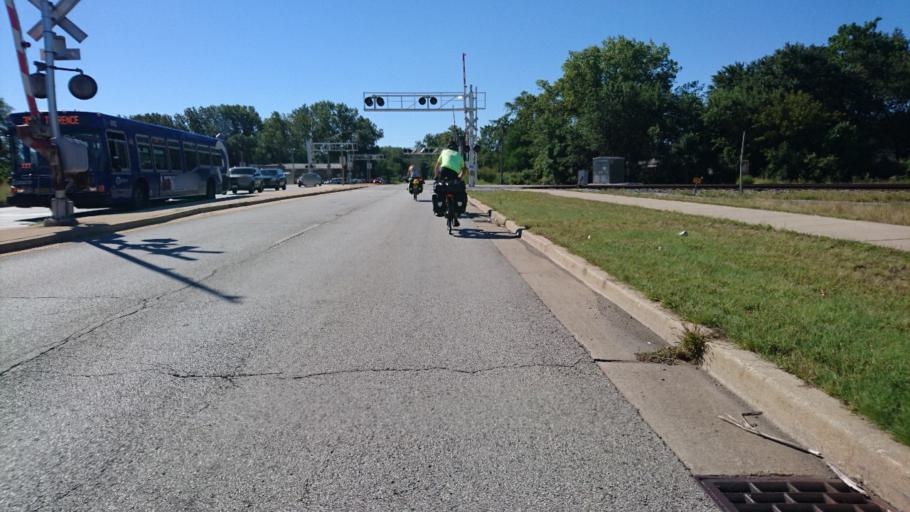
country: US
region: Illinois
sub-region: Cook County
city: Burnham
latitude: 41.6433
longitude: -87.5399
